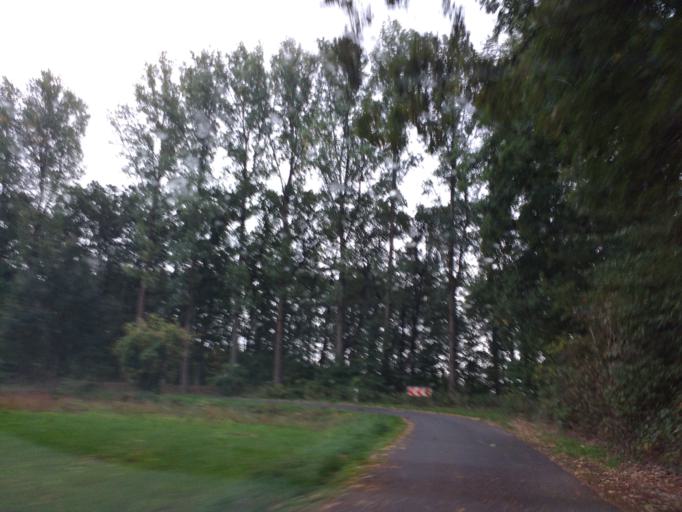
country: DE
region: North Rhine-Westphalia
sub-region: Regierungsbezirk Arnsberg
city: Lippstadt
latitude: 51.7194
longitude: 8.3994
